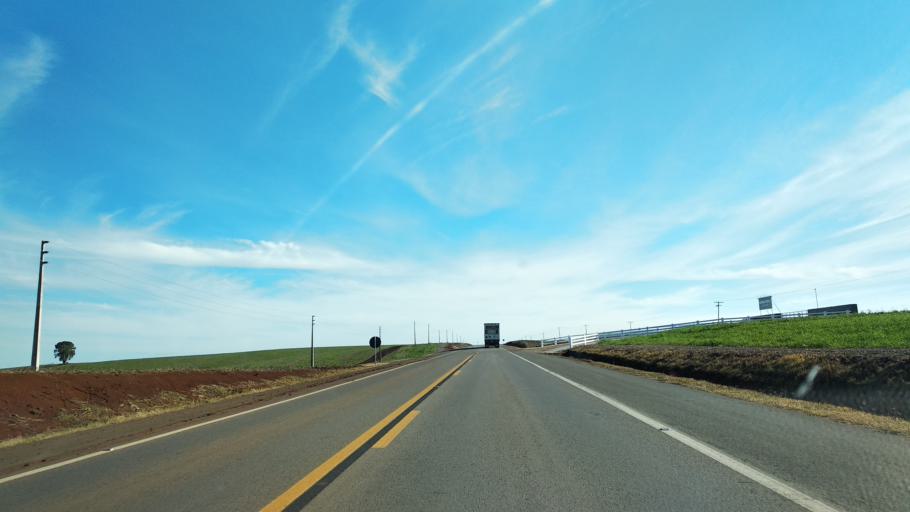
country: BR
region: Santa Catarina
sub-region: Campos Novos
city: Campos Novos
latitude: -27.4868
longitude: -51.3200
